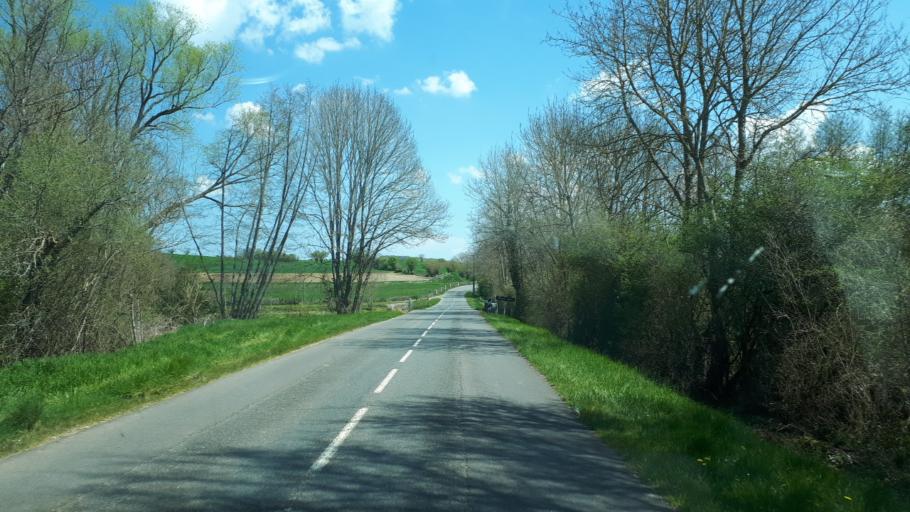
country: FR
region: Centre
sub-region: Departement du Cher
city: Sancerre
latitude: 47.3044
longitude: 2.7106
